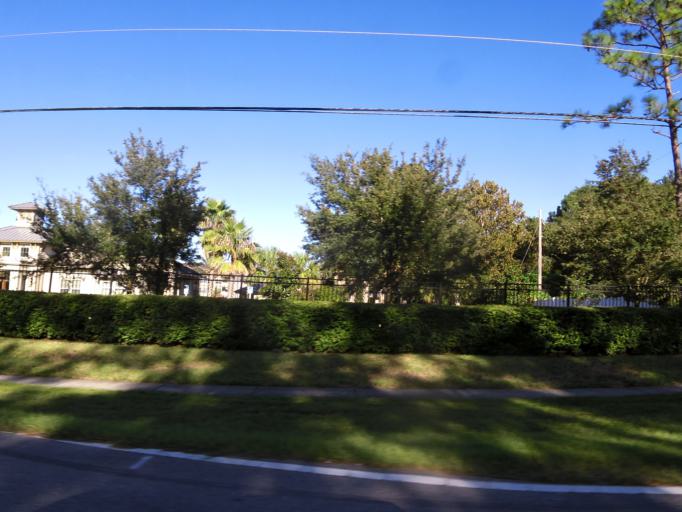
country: US
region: Florida
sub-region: Duval County
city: Neptune Beach
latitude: 30.3174
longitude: -81.4491
